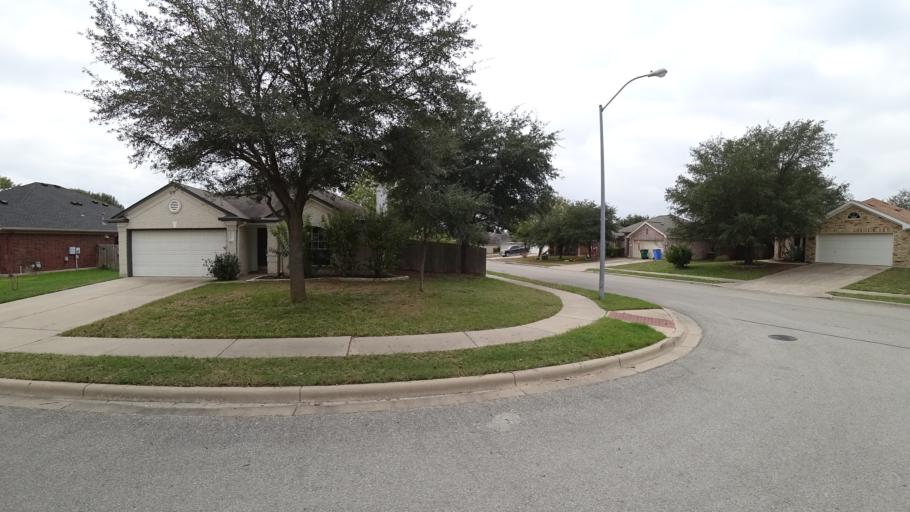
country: US
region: Texas
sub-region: Travis County
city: Pflugerville
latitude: 30.4393
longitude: -97.6079
